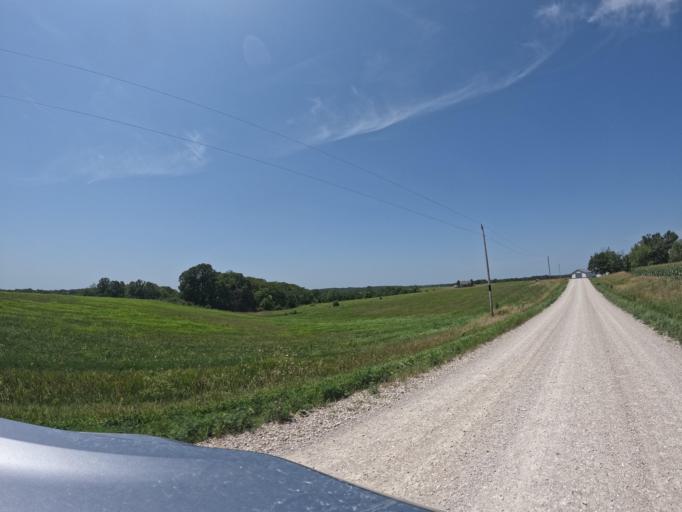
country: US
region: Iowa
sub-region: Henry County
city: Mount Pleasant
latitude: 40.9135
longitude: -91.6578
